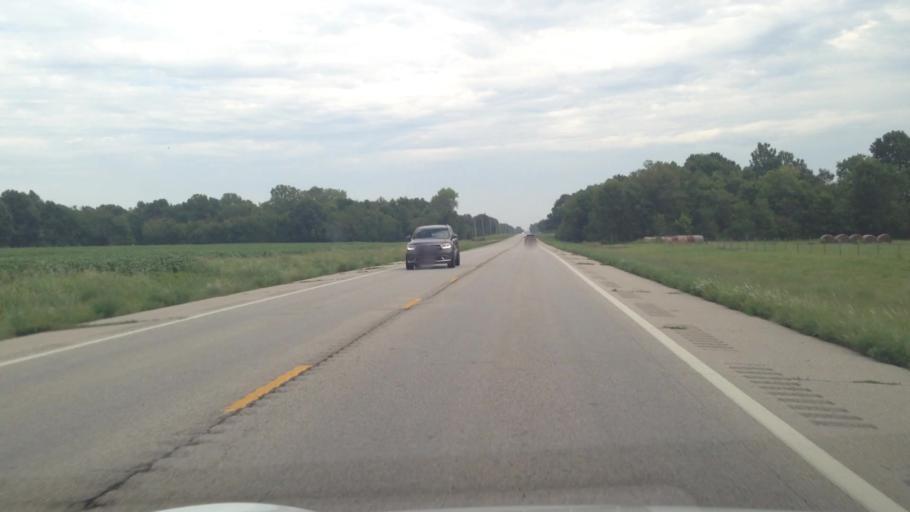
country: US
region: Kansas
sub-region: Crawford County
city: Pittsburg
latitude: 37.3392
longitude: -94.7888
